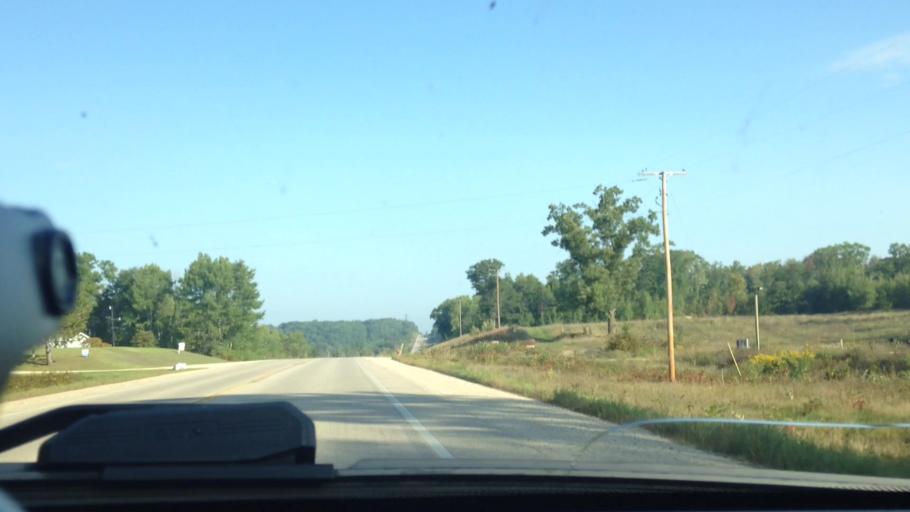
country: US
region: Wisconsin
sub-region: Marinette County
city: Niagara
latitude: 45.4034
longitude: -87.9696
